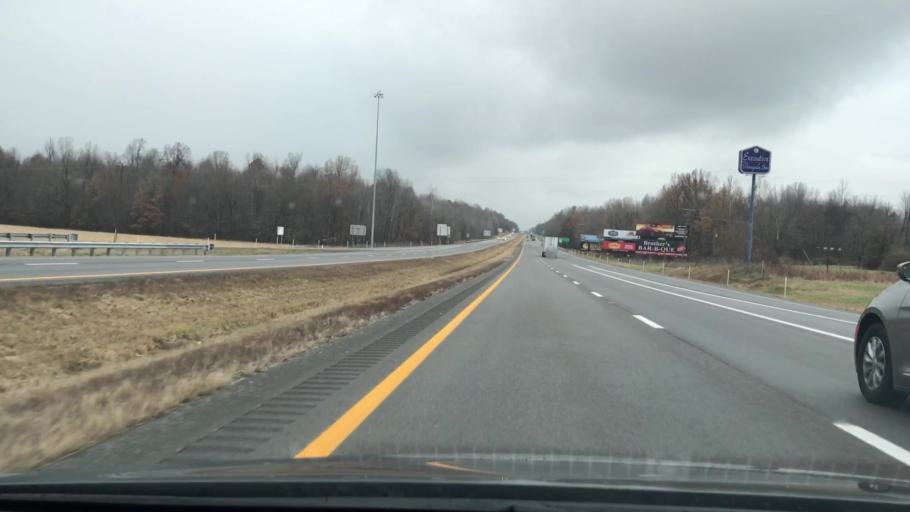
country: US
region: Kentucky
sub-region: Hopkins County
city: Earlington
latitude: 37.2555
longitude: -87.4509
